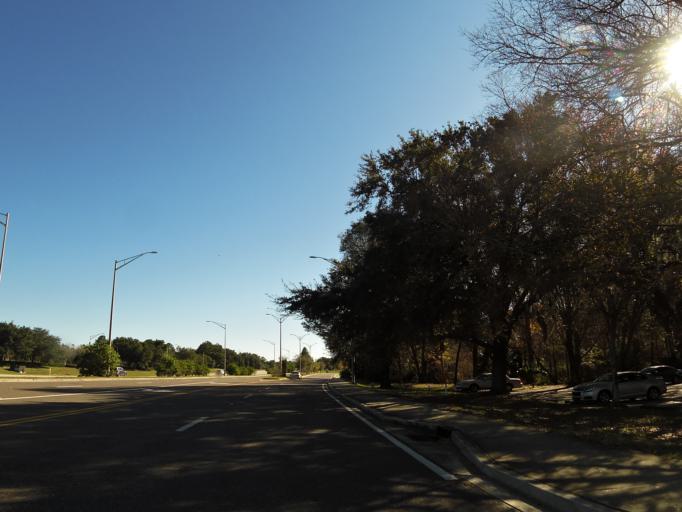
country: US
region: Florida
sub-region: Duval County
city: Jacksonville
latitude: 30.2445
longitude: -81.5525
